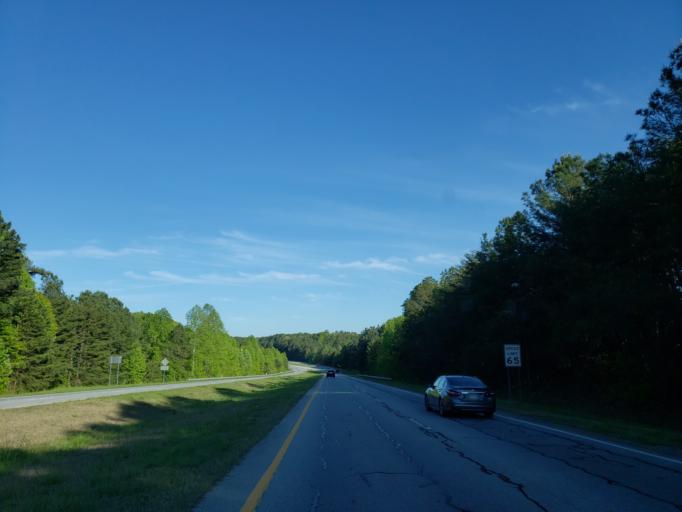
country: US
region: Georgia
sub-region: Paulding County
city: Dallas
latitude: 33.9184
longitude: -84.9281
